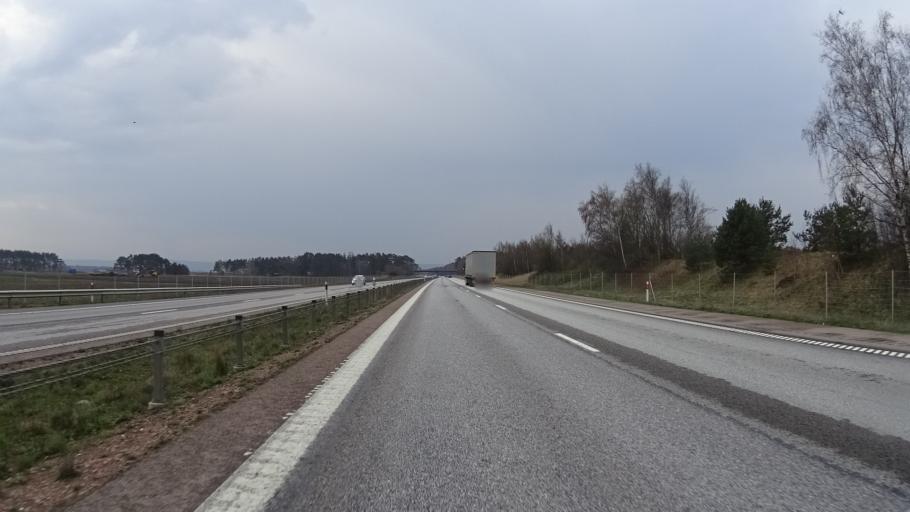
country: SE
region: Halland
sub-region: Laholms Kommun
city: Mellbystrand
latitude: 56.4902
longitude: 12.9531
